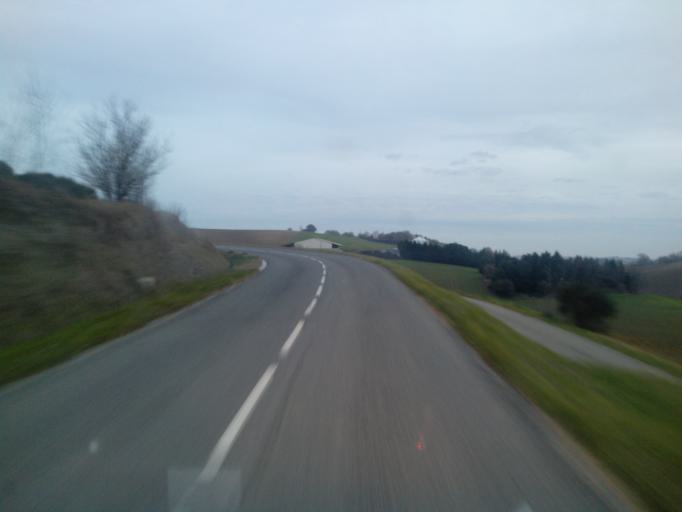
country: FR
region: Languedoc-Roussillon
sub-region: Departement de l'Aude
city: Belpech
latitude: 43.2613
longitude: 1.7514
